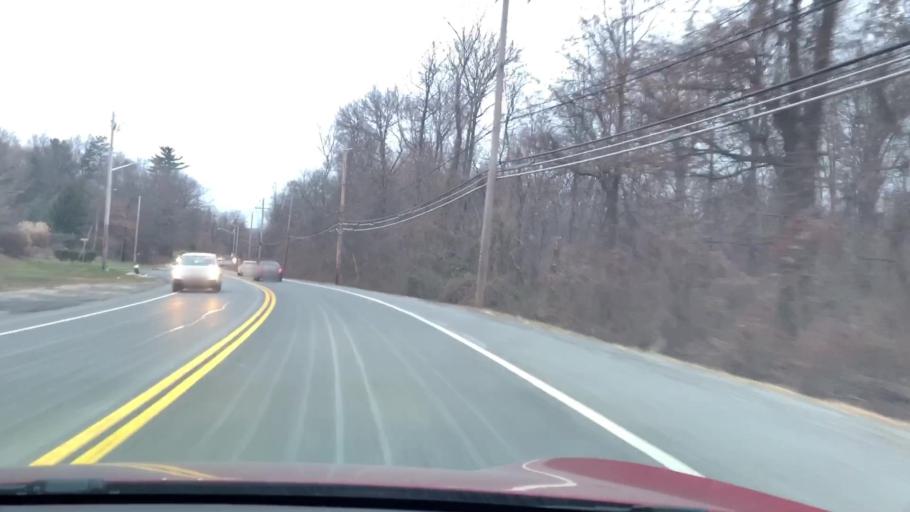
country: US
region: New York
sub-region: Rockland County
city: Sparkill
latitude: 41.0156
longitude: -73.9138
